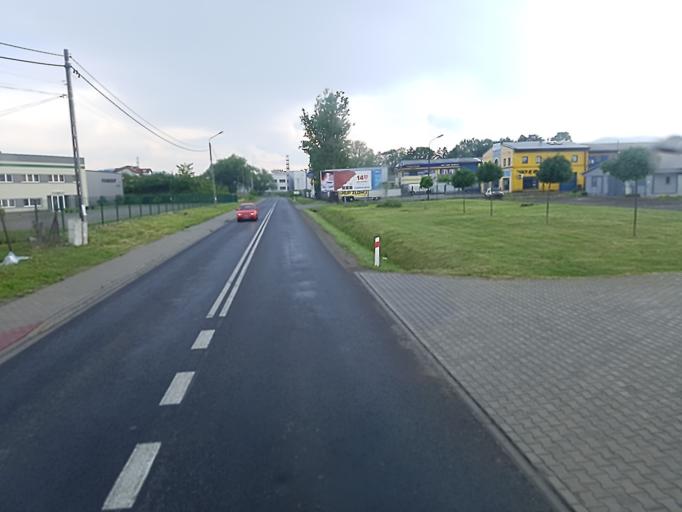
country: PL
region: Silesian Voivodeship
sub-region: Powiat bielski
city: Mazancowice
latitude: 49.8456
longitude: 18.9935
